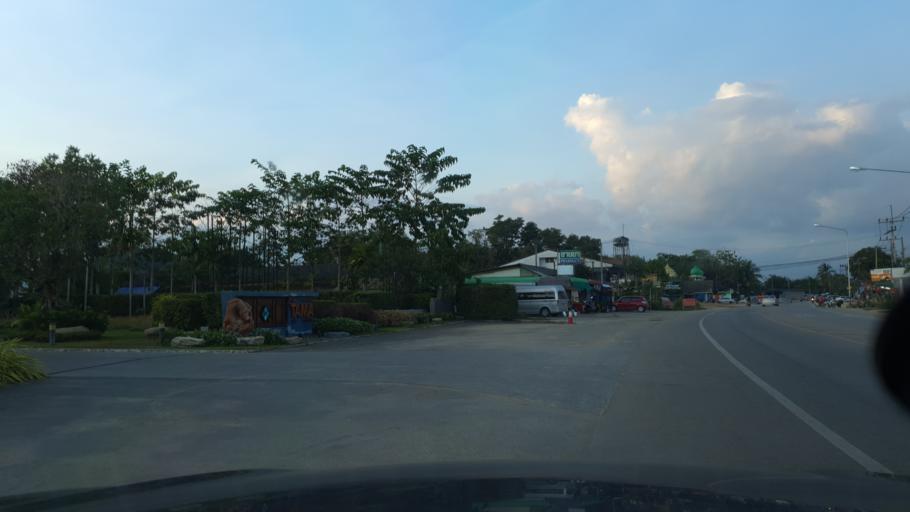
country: TH
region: Phangnga
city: Ban Ao Nang
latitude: 8.0344
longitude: 98.8614
